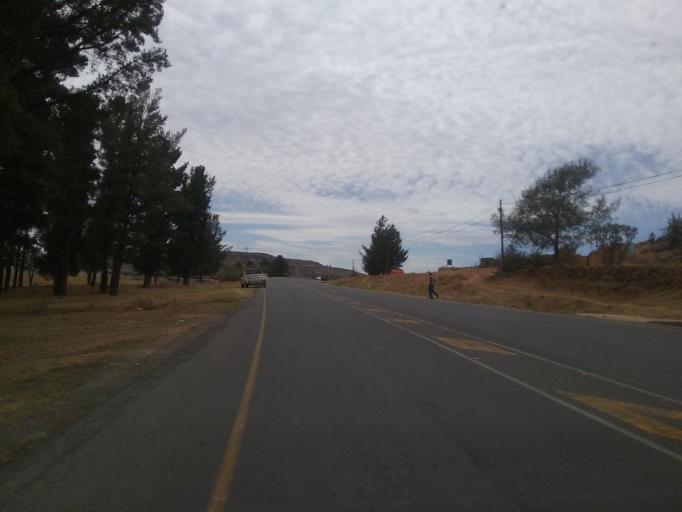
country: LS
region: Maseru
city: Nako
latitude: -29.6288
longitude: 27.4859
